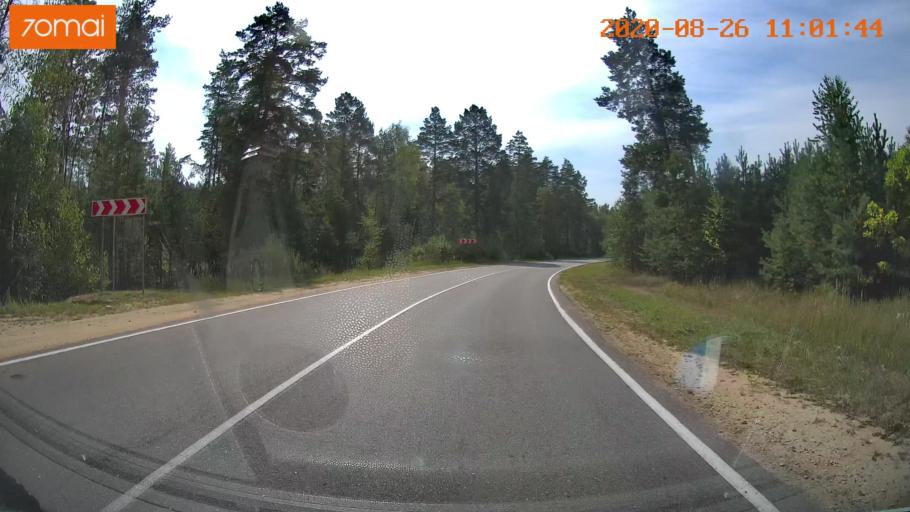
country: RU
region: Rjazan
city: Izhevskoye
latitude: 54.5597
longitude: 41.2274
